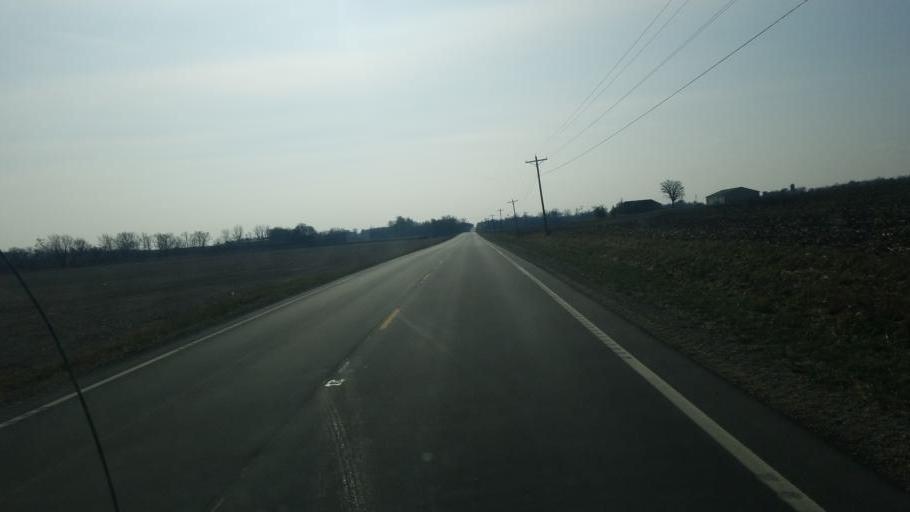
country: US
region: Ohio
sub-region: Mercer County
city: Fort Recovery
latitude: 40.4699
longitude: -84.7844
